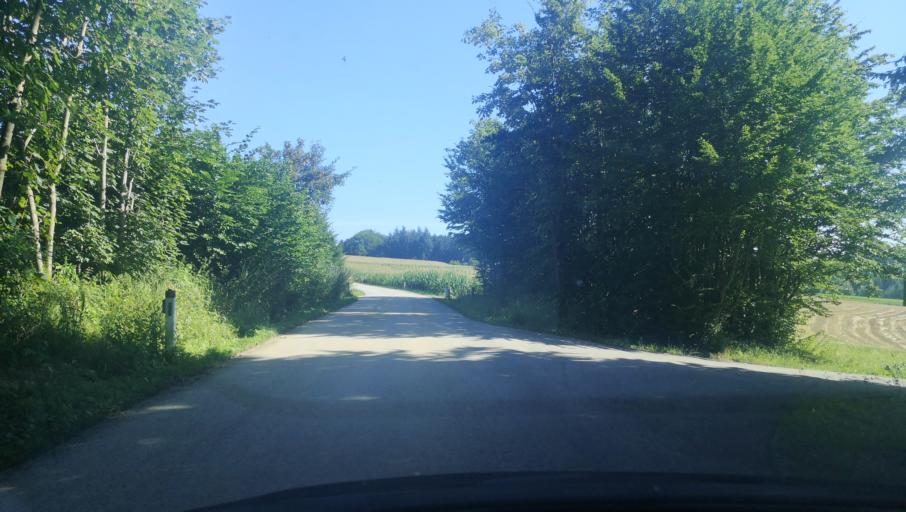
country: AT
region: Lower Austria
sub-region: Politischer Bezirk Melk
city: Blindenmarkt
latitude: 48.1430
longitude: 15.0006
